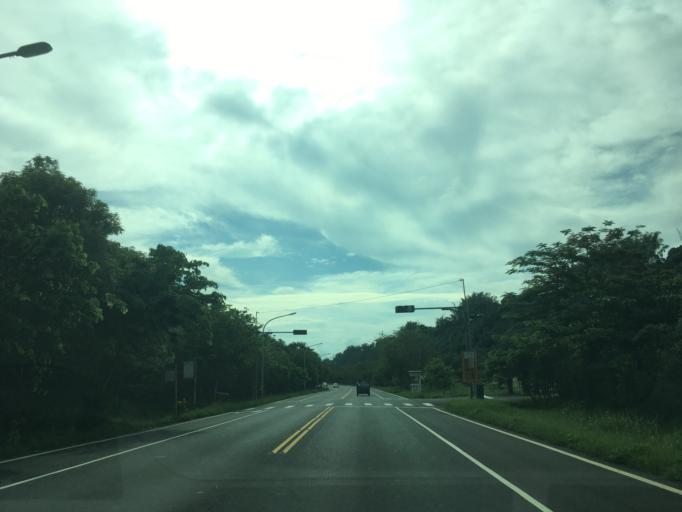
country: TW
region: Taiwan
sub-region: Chiayi
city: Jiayi Shi
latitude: 23.4518
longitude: 120.5664
